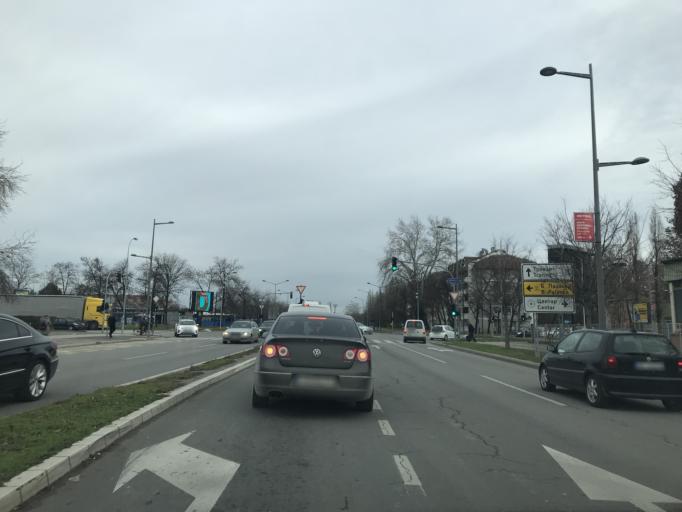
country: RS
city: Veternik
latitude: 45.2439
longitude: 19.7953
